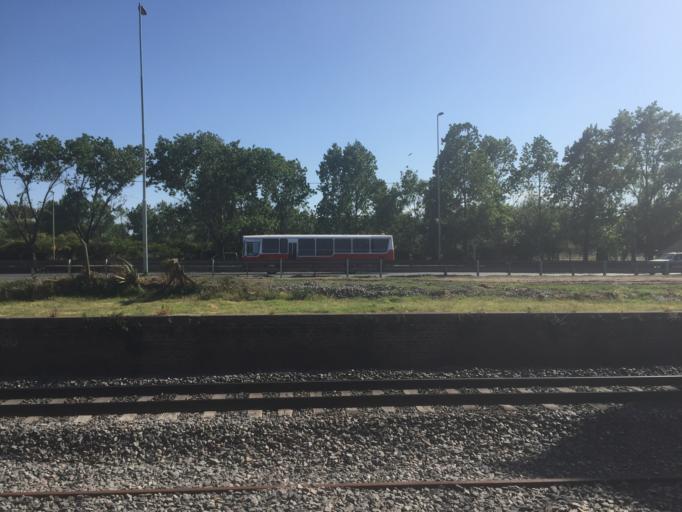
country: AR
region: Buenos Aires F.D.
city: Colegiales
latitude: -34.5422
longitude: -58.4494
